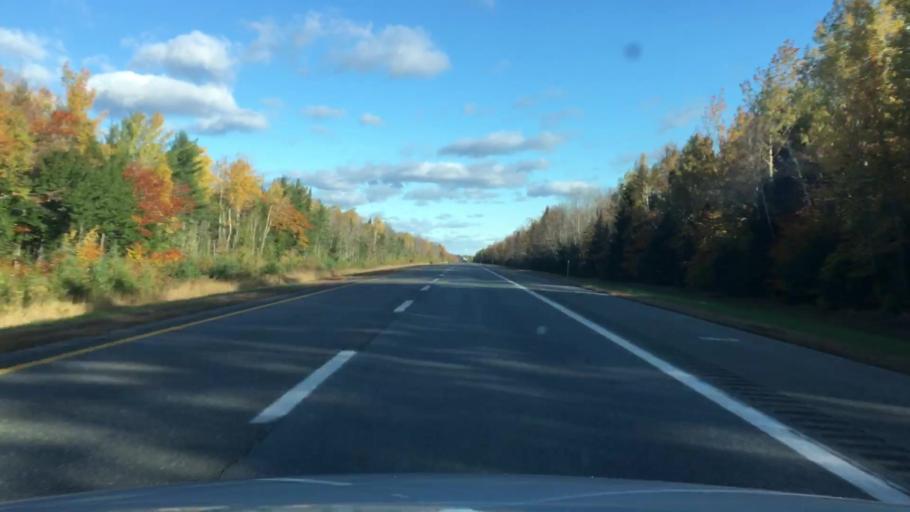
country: US
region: Maine
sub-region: Penobscot County
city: Greenbush
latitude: 45.0785
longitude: -68.6918
